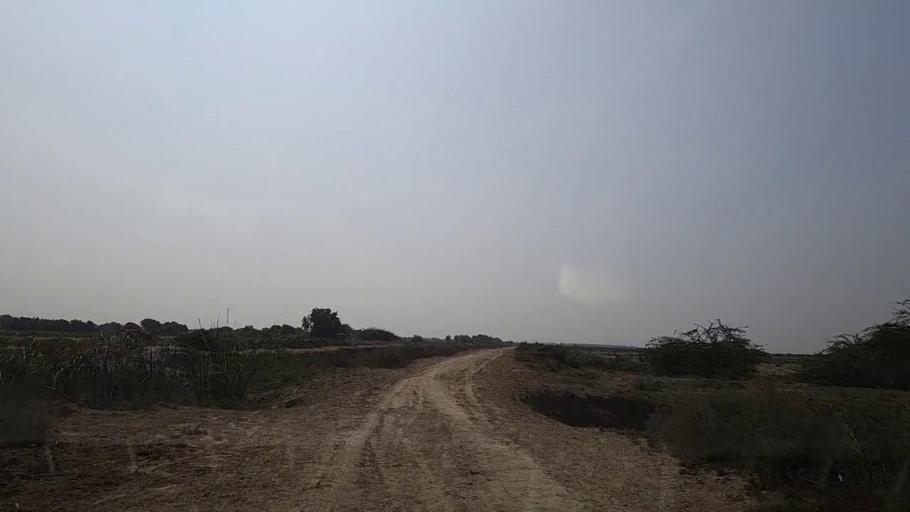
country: PK
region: Sindh
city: Mirpur Sakro
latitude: 24.5460
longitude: 67.7897
